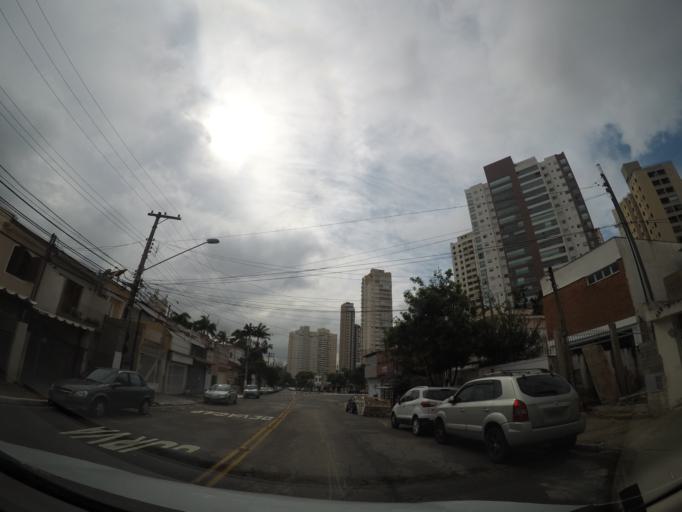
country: BR
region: Sao Paulo
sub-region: Sao Paulo
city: Sao Paulo
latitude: -23.5887
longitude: -46.6251
